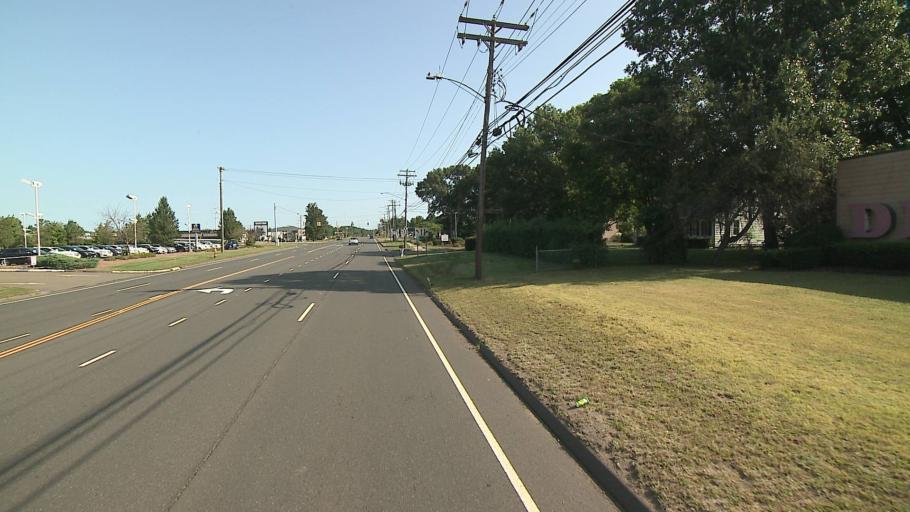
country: US
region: Connecticut
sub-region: New Haven County
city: North Haven
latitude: 41.4179
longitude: -72.8404
